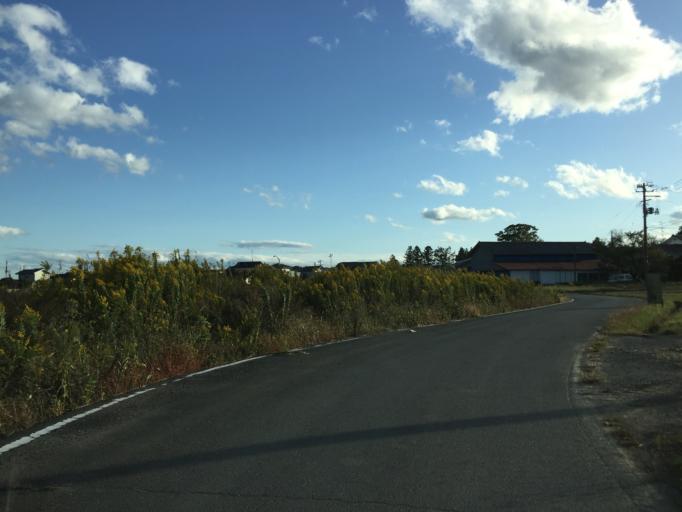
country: JP
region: Miyagi
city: Marumori
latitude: 37.7909
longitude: 140.9530
